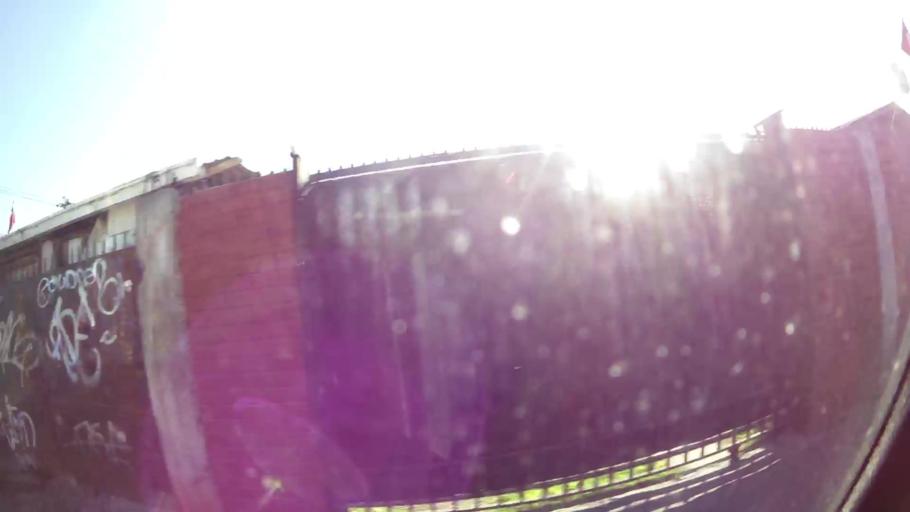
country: CL
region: Santiago Metropolitan
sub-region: Provincia de Santiago
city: Lo Prado
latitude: -33.4890
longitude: -70.7645
